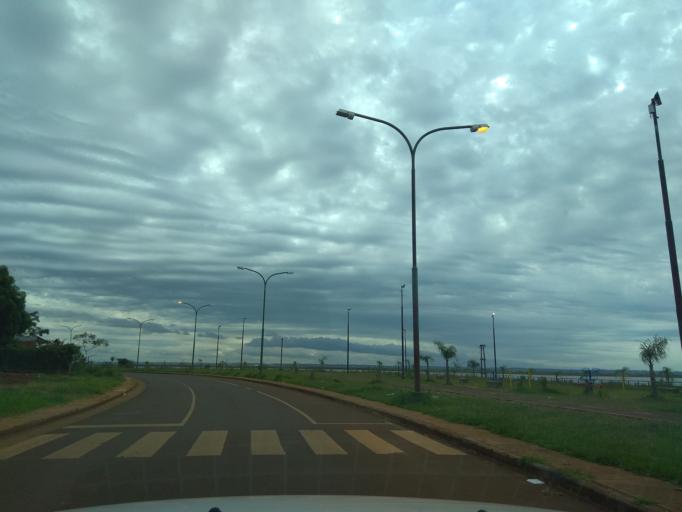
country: AR
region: Misiones
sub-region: Departamento de Capital
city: Posadas
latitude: -27.4168
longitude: -55.8978
